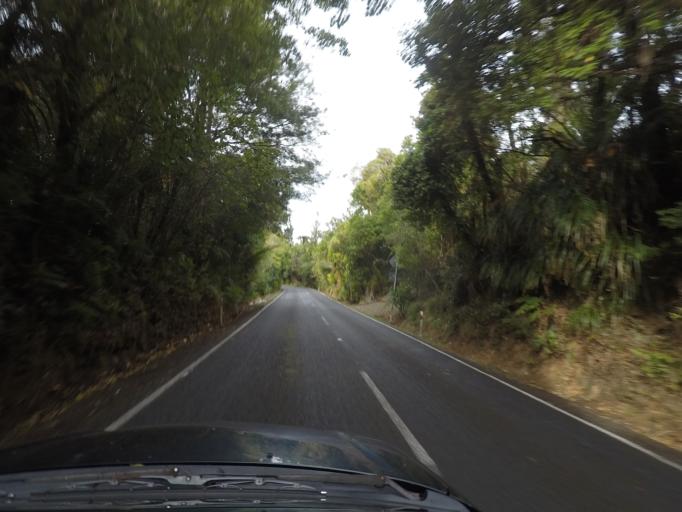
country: NZ
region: Auckland
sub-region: Auckland
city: Titirangi
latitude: -36.9429
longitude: 174.5835
